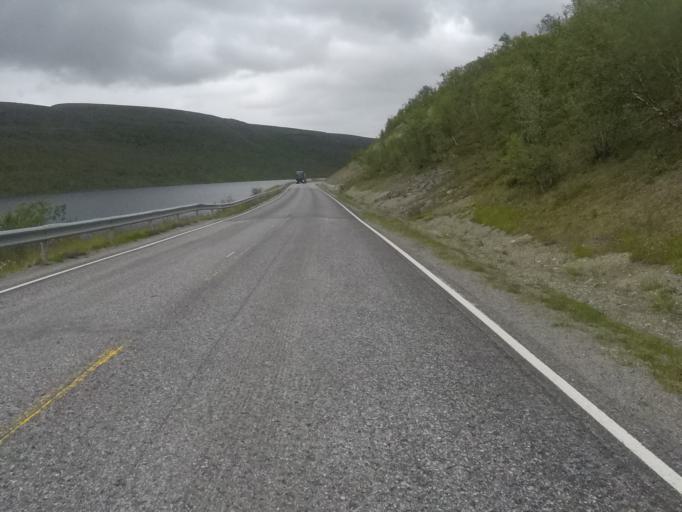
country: NO
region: Finnmark Fylke
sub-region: Alta
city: Alta
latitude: 69.7021
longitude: 23.4090
